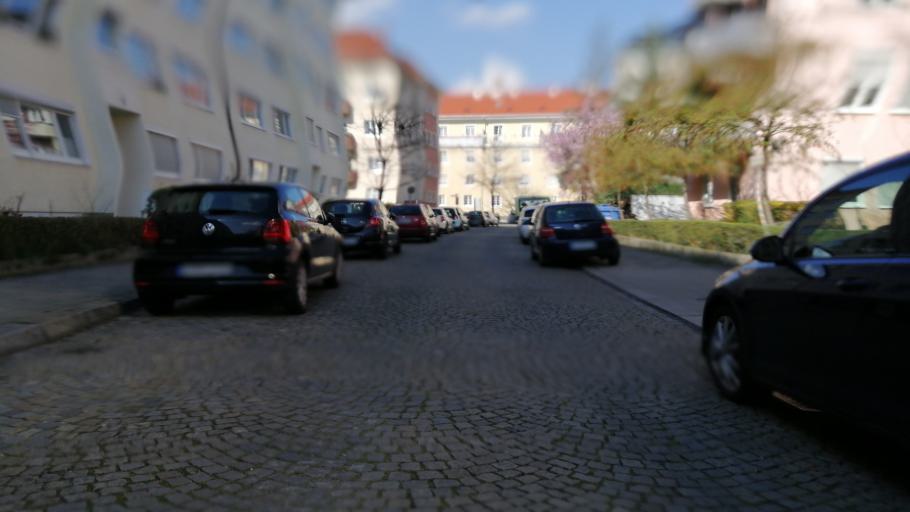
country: DE
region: Bavaria
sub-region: Upper Bavaria
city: Munich
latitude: 48.1686
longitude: 11.5792
